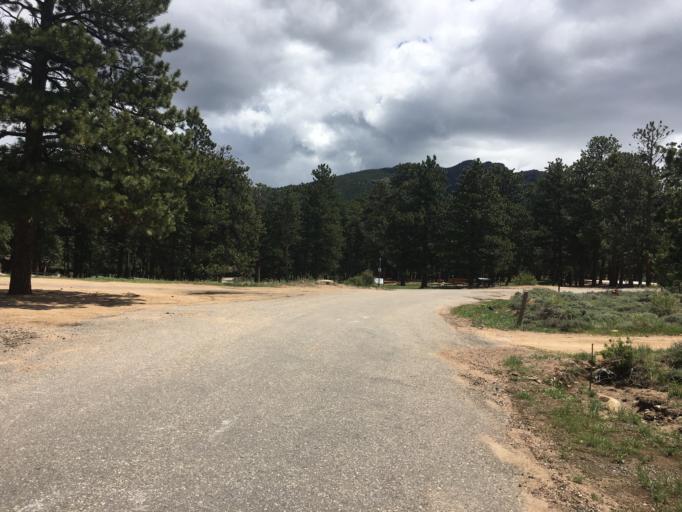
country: US
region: Colorado
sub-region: Larimer County
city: Estes Park
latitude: 40.3425
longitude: -105.5798
